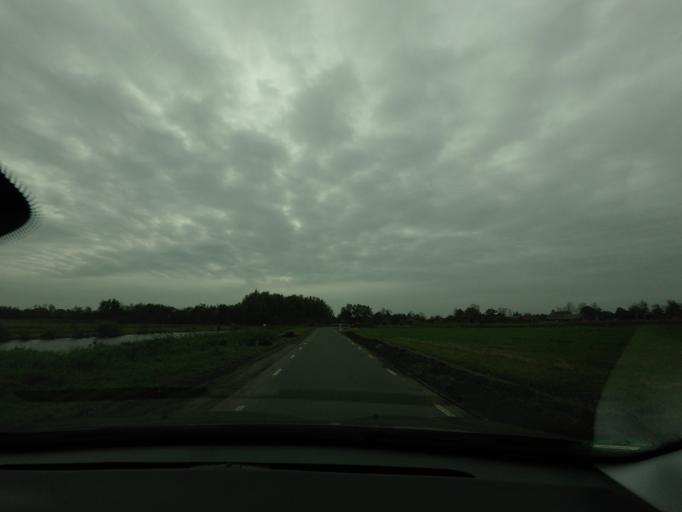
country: NL
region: Overijssel
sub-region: Gemeente Steenwijkerland
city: Blokzijl
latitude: 52.7737
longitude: 5.9682
